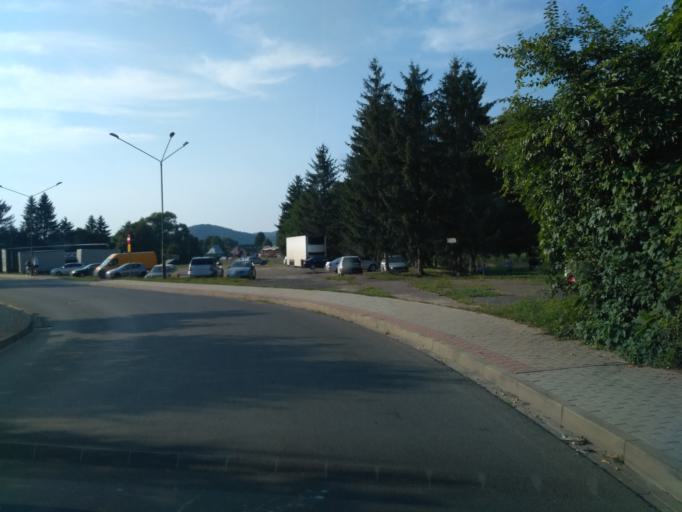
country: PL
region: Subcarpathian Voivodeship
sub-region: Powiat sanocki
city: Sanok
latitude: 49.5715
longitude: 22.2063
